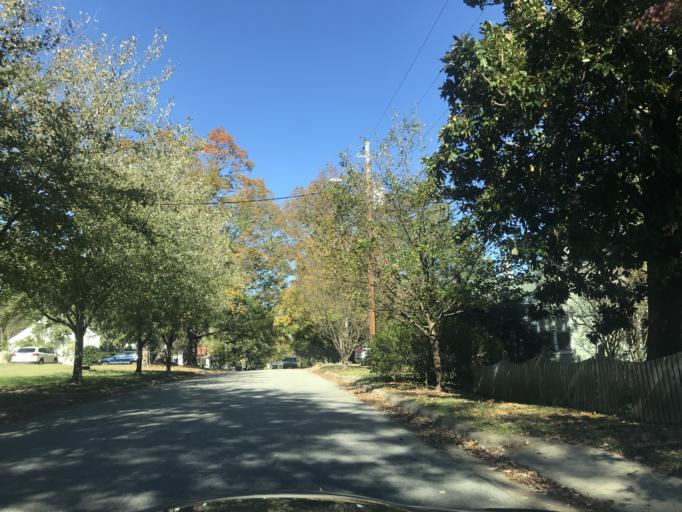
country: US
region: North Carolina
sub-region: Wake County
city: Raleigh
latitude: 35.7863
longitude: -78.6303
